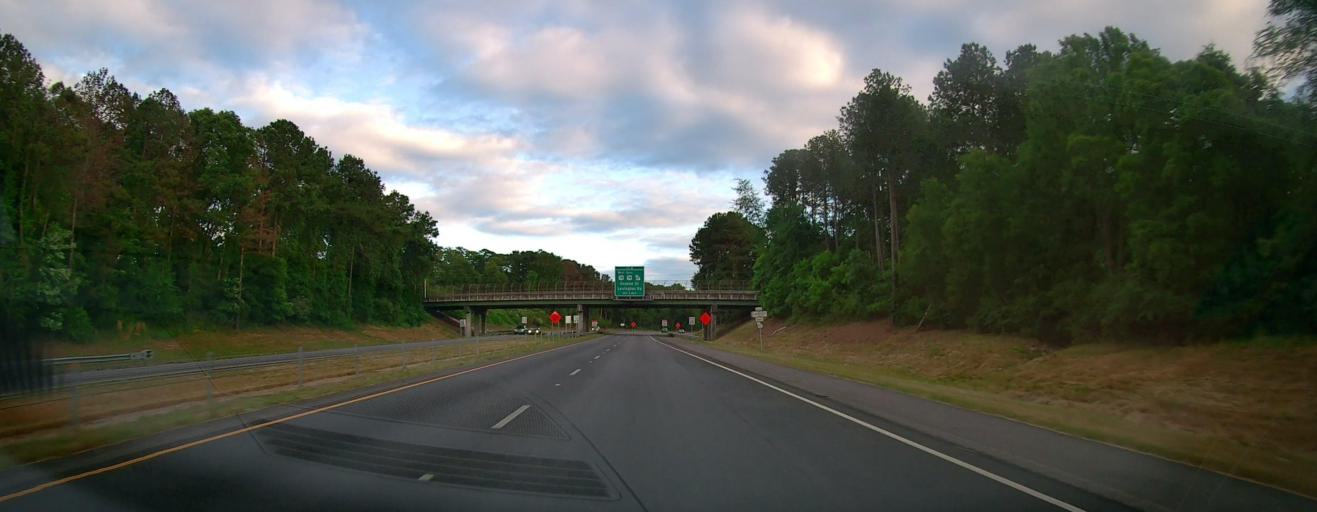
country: US
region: Georgia
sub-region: Clarke County
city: Athens
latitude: 33.9575
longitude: -83.3507
